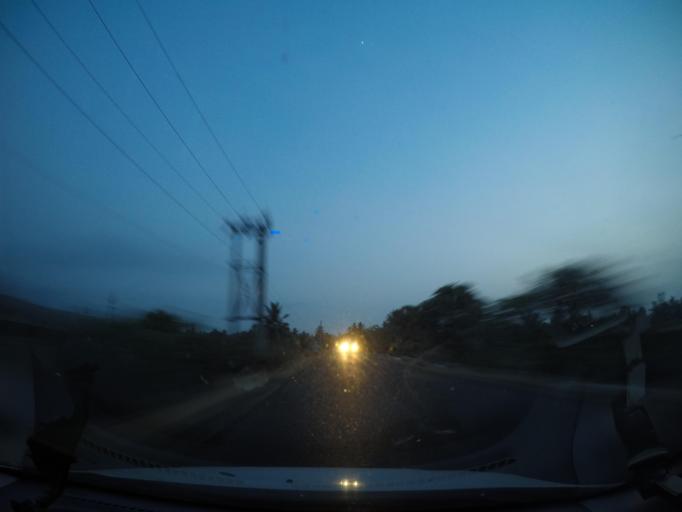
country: IN
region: Andhra Pradesh
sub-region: West Godavari
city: Tadepallegudem
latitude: 16.7781
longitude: 81.4242
